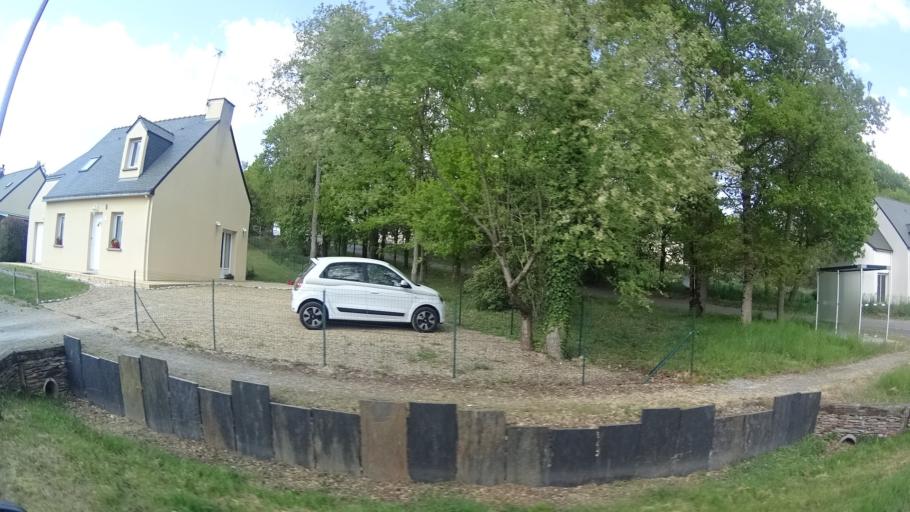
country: FR
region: Pays de la Loire
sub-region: Departement de la Loire-Atlantique
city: Saint-Nicolas-de-Redon
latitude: 47.6385
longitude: -2.0681
